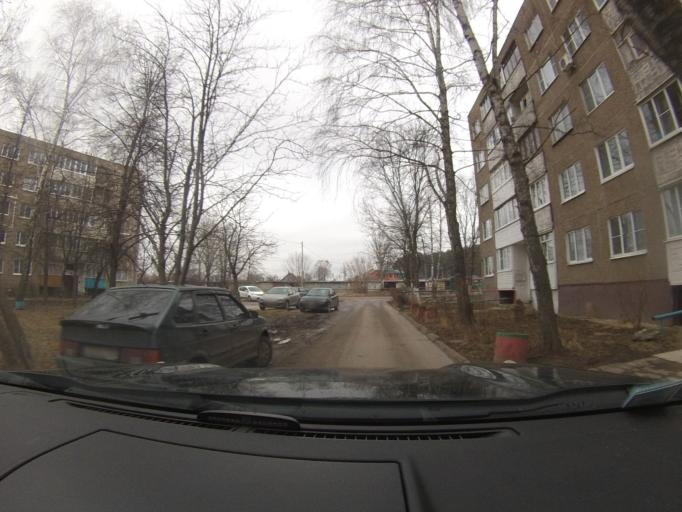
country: RU
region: Moskovskaya
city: Peski
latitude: 55.2762
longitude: 38.7512
